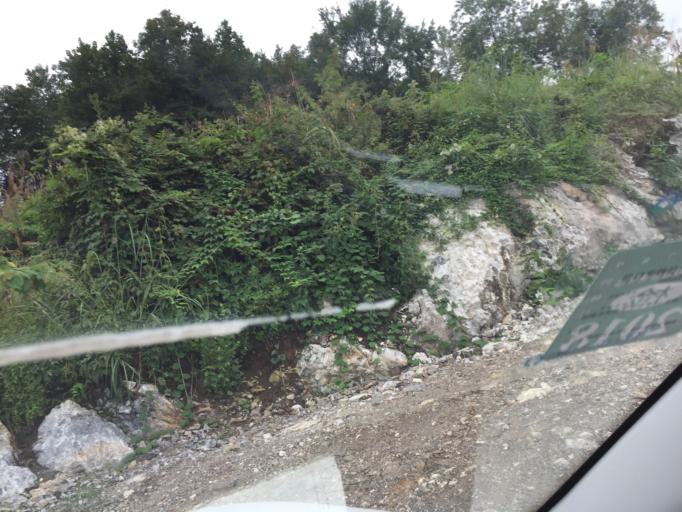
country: CN
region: Guizhou Sheng
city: Yantang
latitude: 28.2056
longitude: 108.0878
